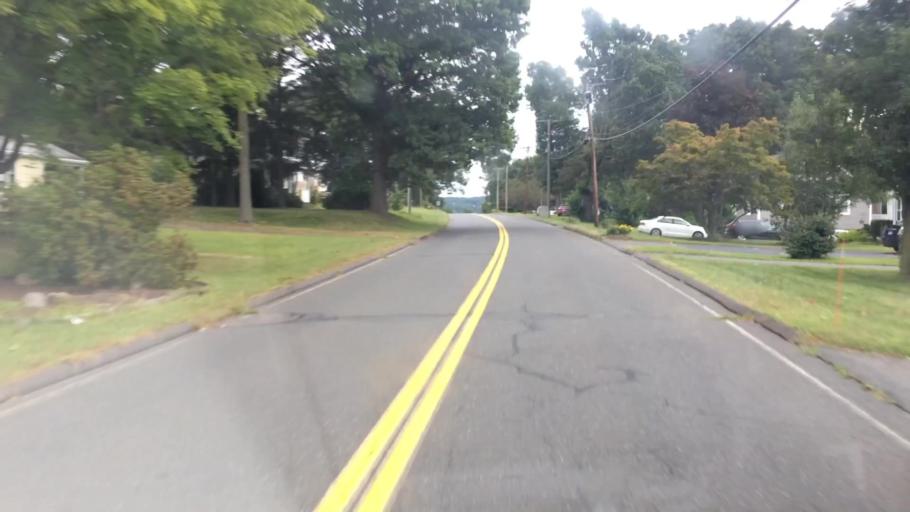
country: US
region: Connecticut
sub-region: Middlesex County
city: Cromwell
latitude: 41.6539
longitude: -72.6395
